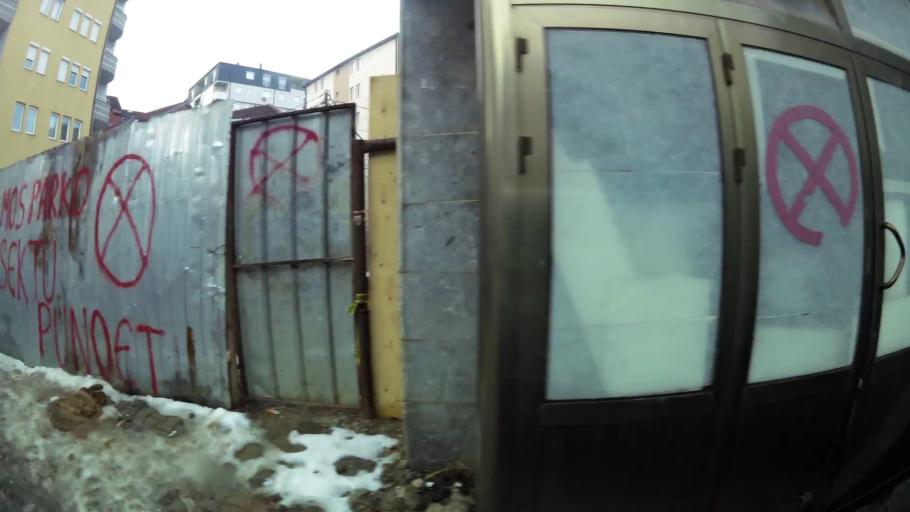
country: XK
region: Pristina
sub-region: Komuna e Prishtines
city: Pristina
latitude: 42.6629
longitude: 21.1673
